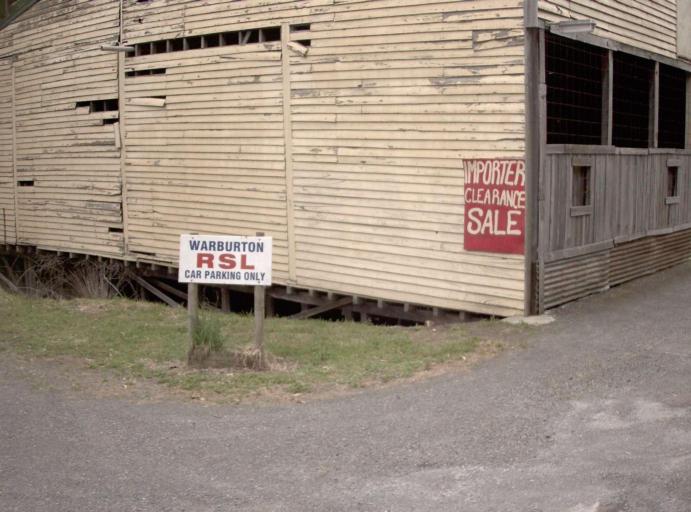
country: AU
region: Victoria
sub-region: Yarra Ranges
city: Millgrove
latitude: -37.7550
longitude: 145.6821
